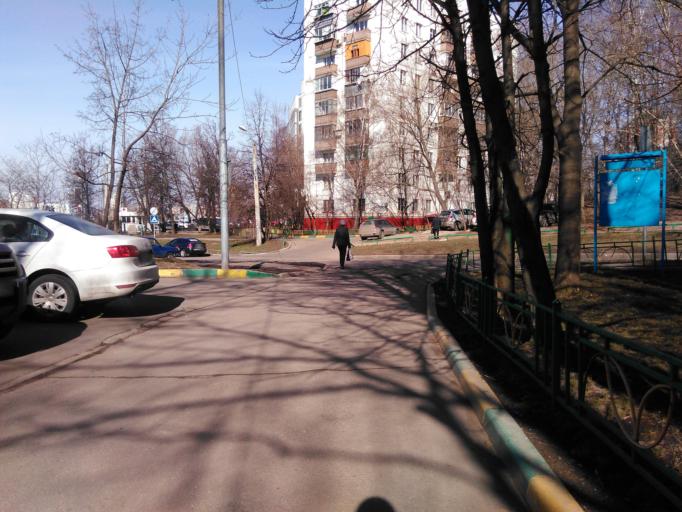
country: RU
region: Moscow
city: Troparevo
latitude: 55.6680
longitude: 37.5035
